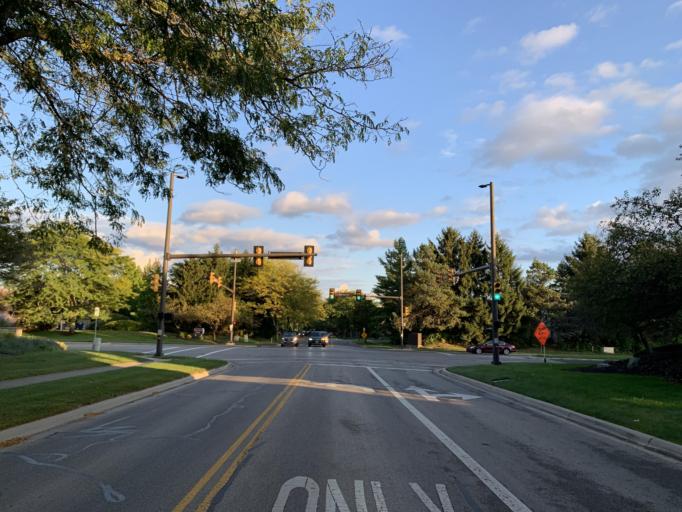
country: US
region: Ohio
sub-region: Franklin County
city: Dublin
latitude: 40.1130
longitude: -83.1557
